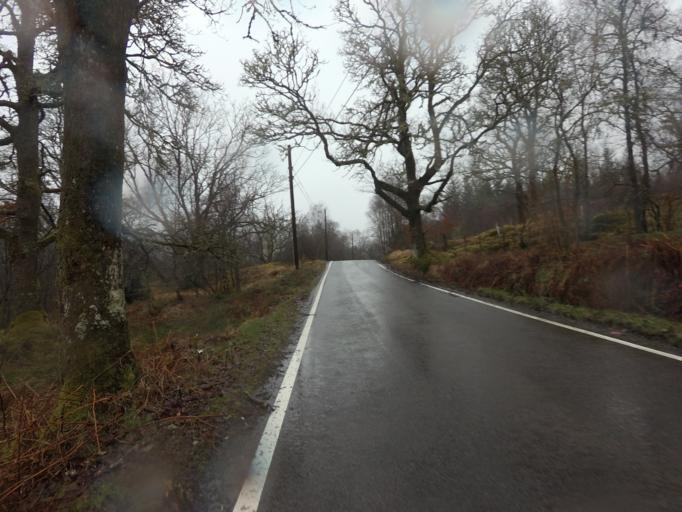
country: GB
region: Scotland
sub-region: West Dunbartonshire
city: Balloch
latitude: 56.1963
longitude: -4.5204
